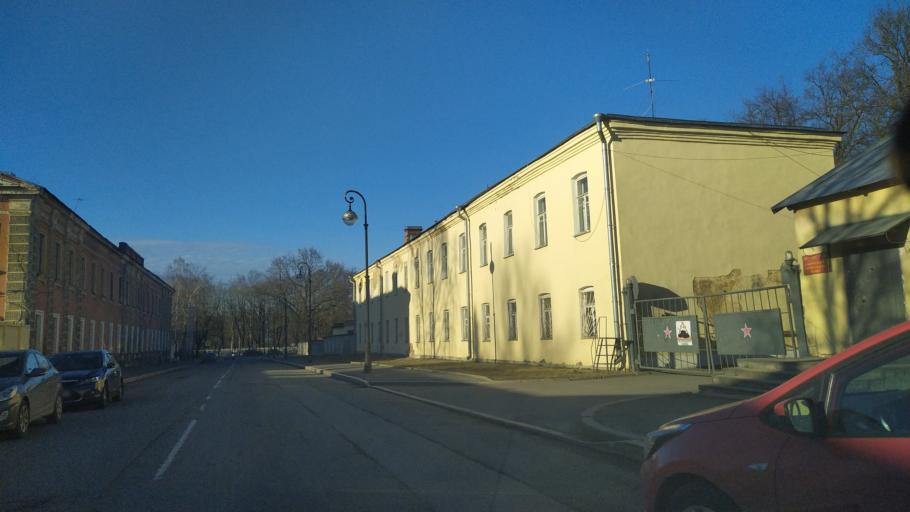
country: RU
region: St.-Petersburg
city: Pushkin
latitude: 59.7068
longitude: 30.3907
